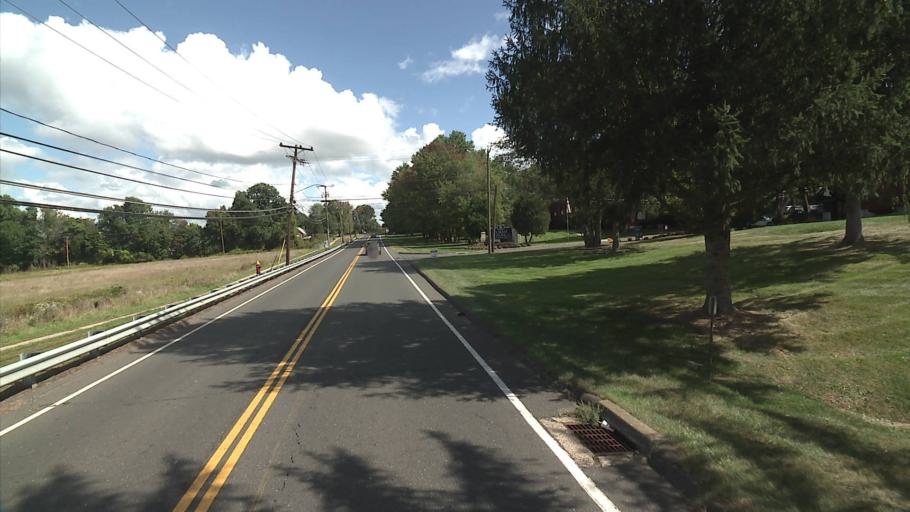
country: US
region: Connecticut
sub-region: Middlesex County
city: Cromwell
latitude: 41.6538
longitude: -72.6466
